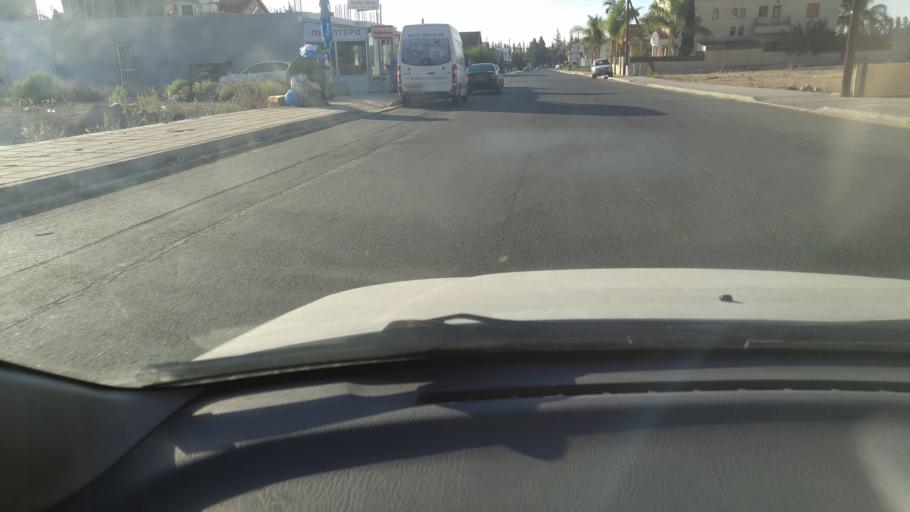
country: CY
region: Limassol
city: Ypsonas
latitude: 34.6571
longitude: 32.9734
